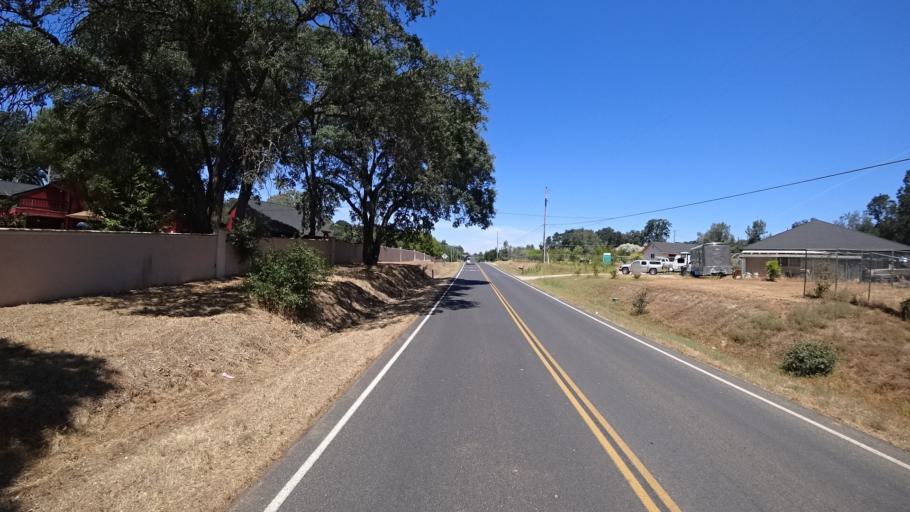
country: US
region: California
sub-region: Calaveras County
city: Rancho Calaveras
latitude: 38.1188
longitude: -120.8618
